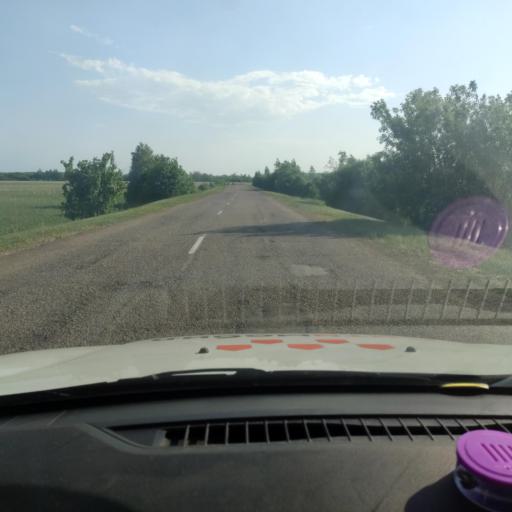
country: RU
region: Bashkortostan
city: Asanovo
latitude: 54.9889
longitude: 55.5654
